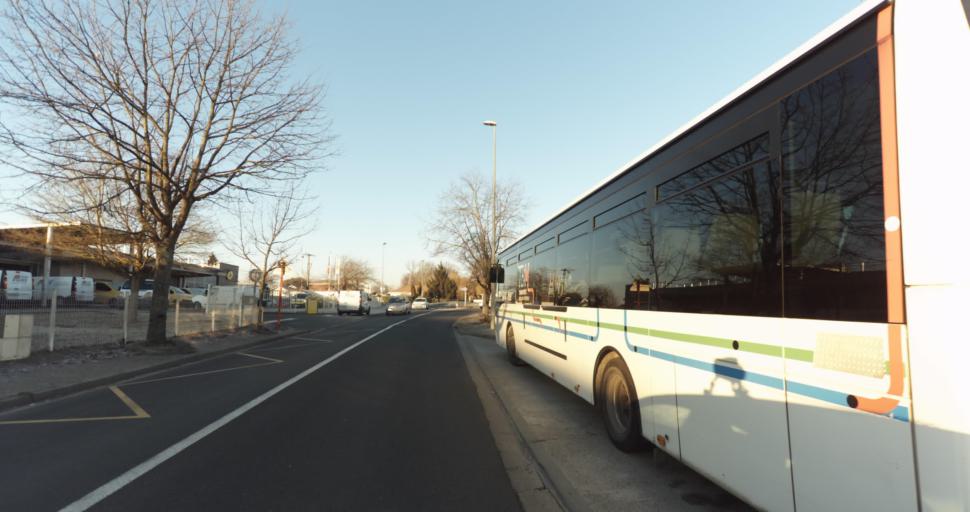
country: FR
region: Aquitaine
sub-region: Departement de la Gironde
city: Ambares-et-Lagrave
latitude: 44.9133
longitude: -0.4927
